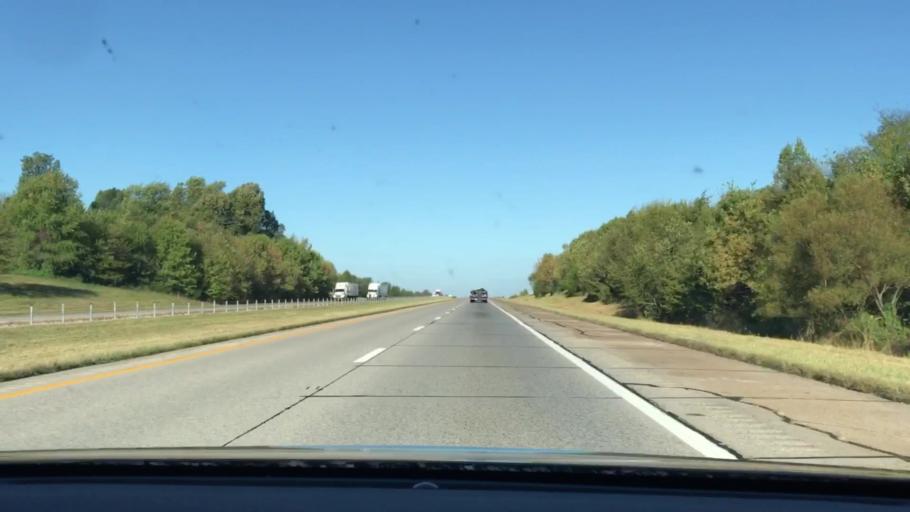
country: US
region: Kentucky
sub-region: Caldwell County
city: Princeton
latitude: 36.9837
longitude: -87.9194
